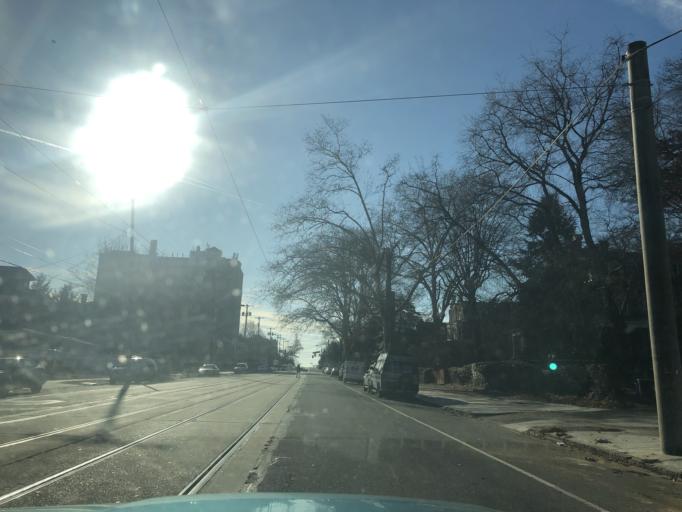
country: US
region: Pennsylvania
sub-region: Delaware County
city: Millbourne
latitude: 39.9828
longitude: -75.2470
